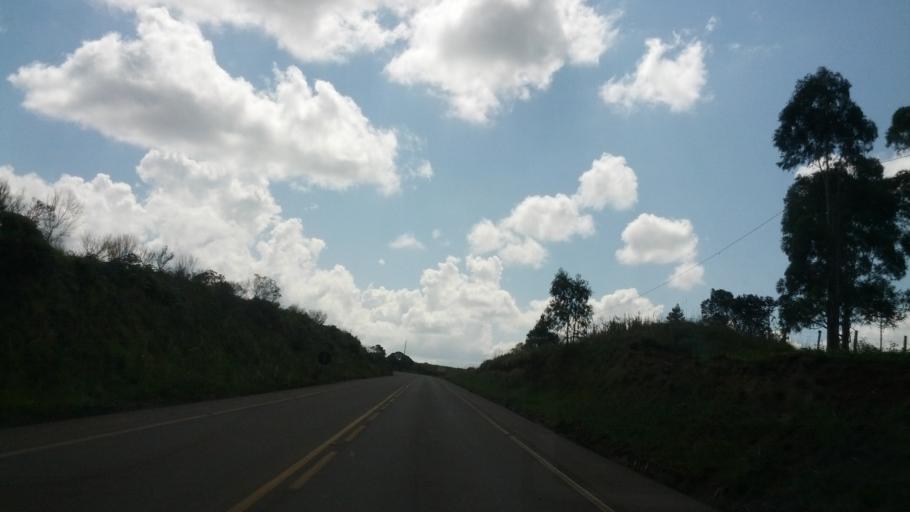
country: BR
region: Rio Grande do Sul
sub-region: Vacaria
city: Estrela
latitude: -27.7972
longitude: -50.8832
